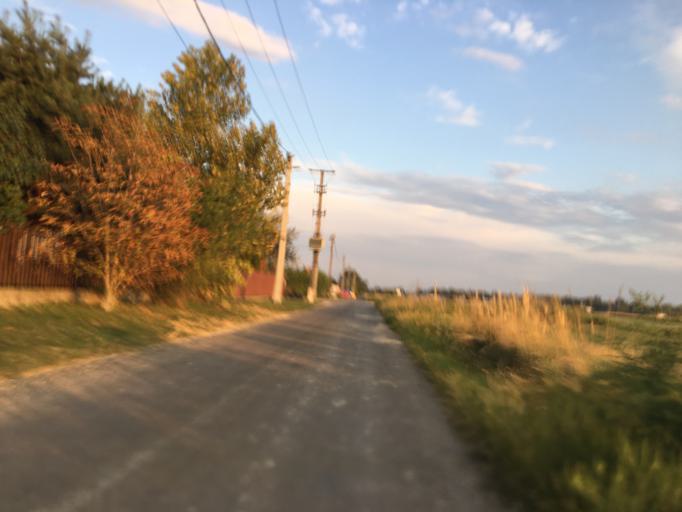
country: HU
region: Pest
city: Szigetszentmiklos
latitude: 47.3439
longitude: 19.0184
